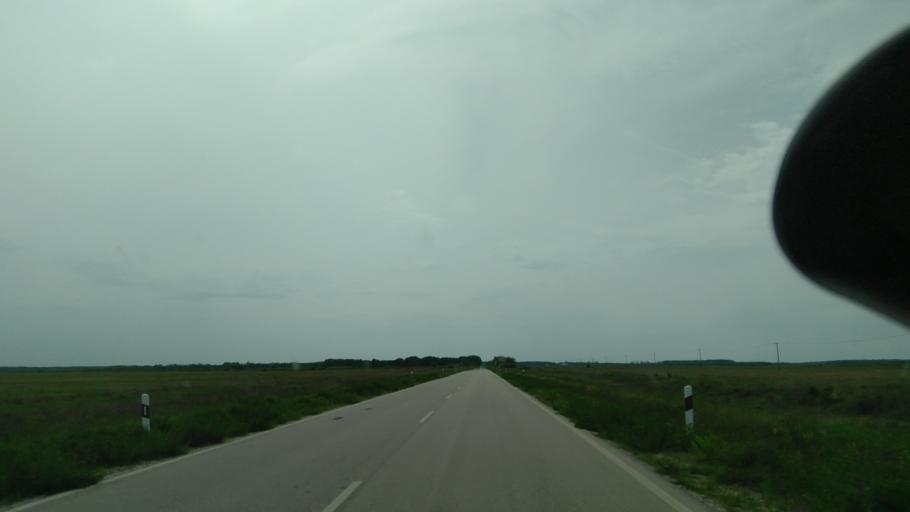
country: HU
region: Bekes
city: Mehkerek
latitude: 46.8669
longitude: 21.4890
